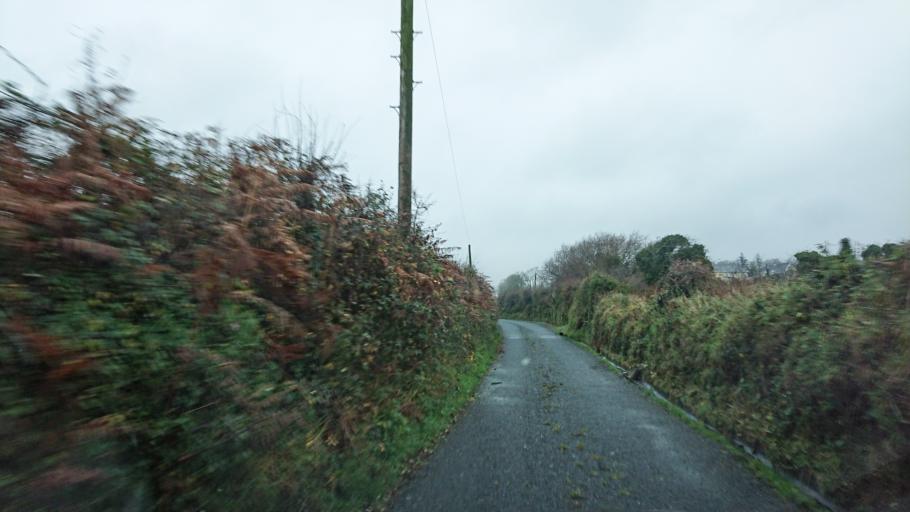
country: IE
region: Munster
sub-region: Waterford
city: Tra Mhor
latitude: 52.2019
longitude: -7.1763
